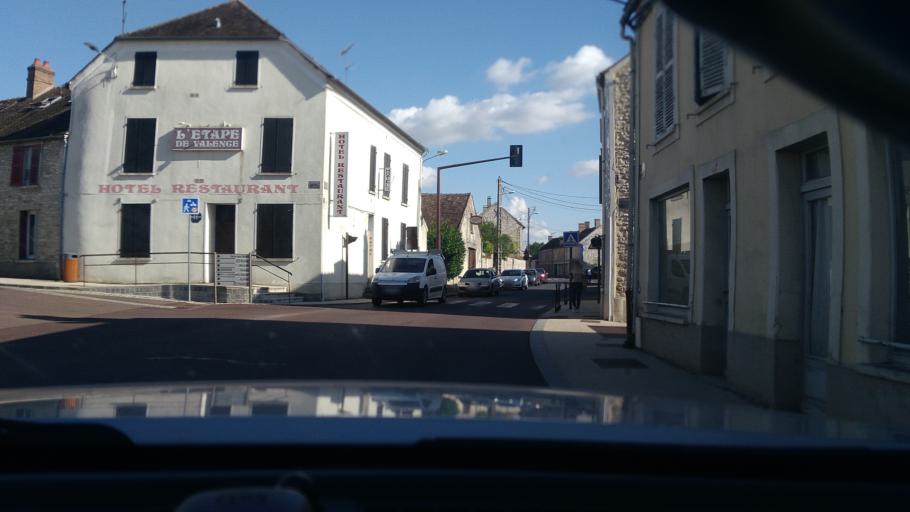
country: FR
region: Ile-de-France
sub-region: Departement de Seine-et-Marne
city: La Grande-Paroisse
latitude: 48.4441
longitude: 2.8900
